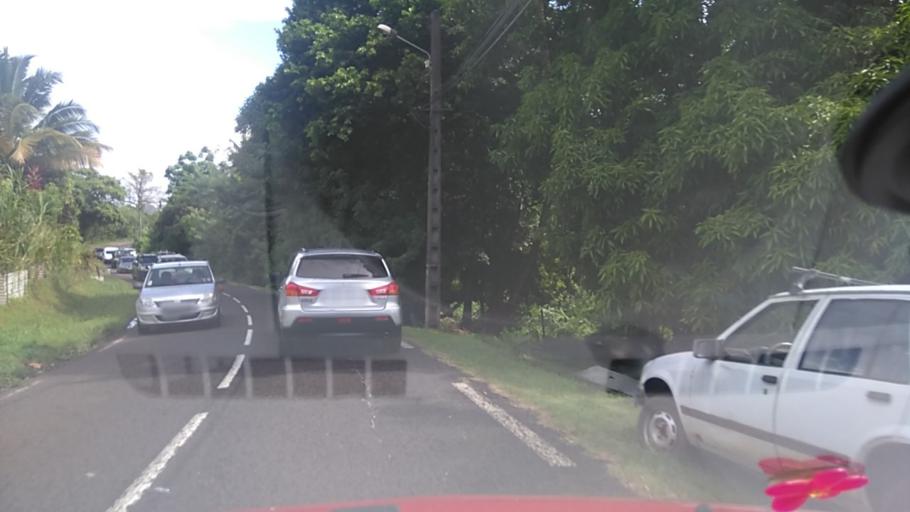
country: MQ
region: Martinique
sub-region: Martinique
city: Le Francois
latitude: 14.5878
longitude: -60.9236
